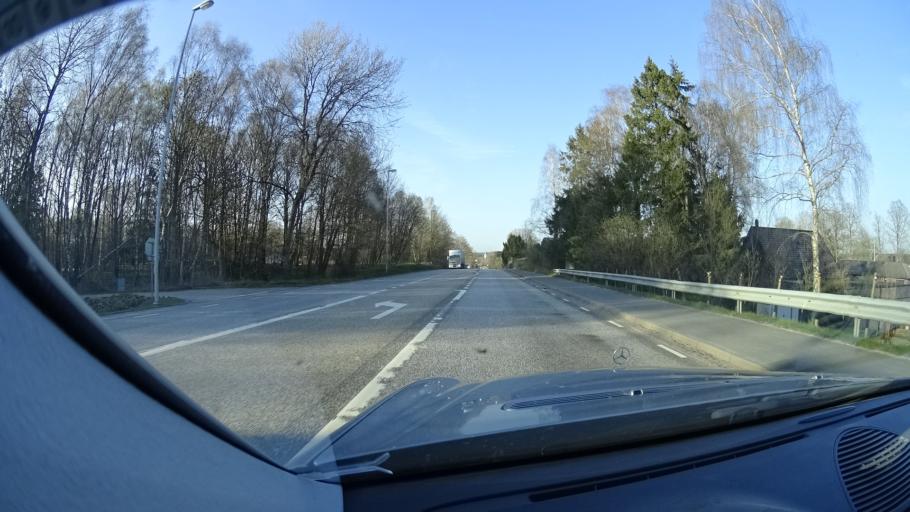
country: SE
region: Skane
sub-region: Hoors Kommun
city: Satofta
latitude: 55.9207
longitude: 13.5402
